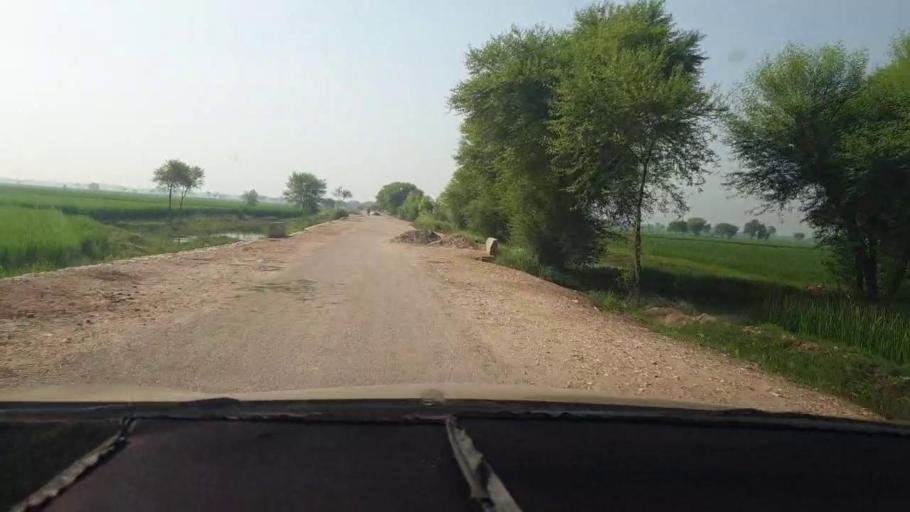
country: PK
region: Sindh
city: Kambar
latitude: 27.6239
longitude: 68.0896
